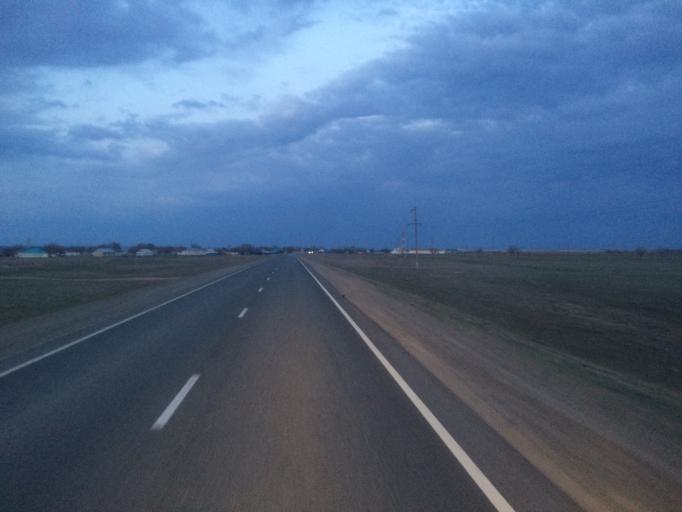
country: KZ
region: Aqtoebe
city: Martuk
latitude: 50.6402
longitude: 56.6832
